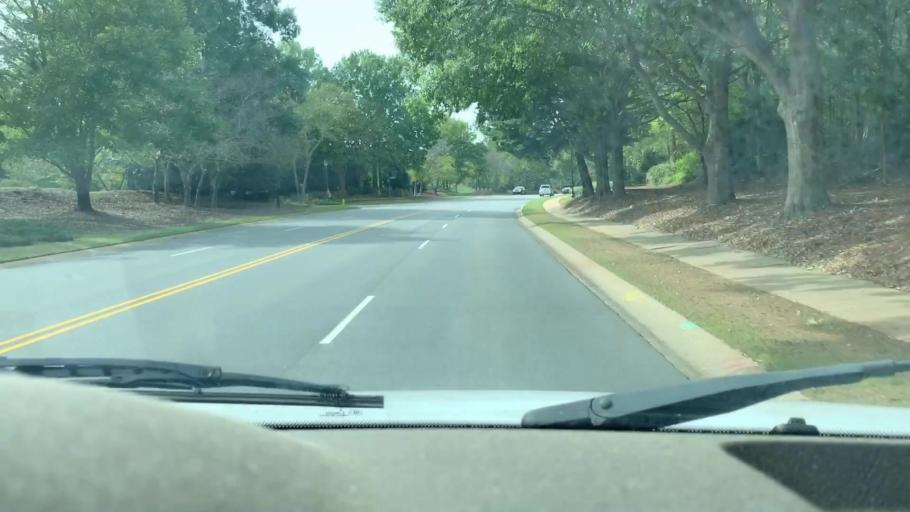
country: US
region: North Carolina
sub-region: Mecklenburg County
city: Cornelius
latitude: 35.4758
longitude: -80.9014
